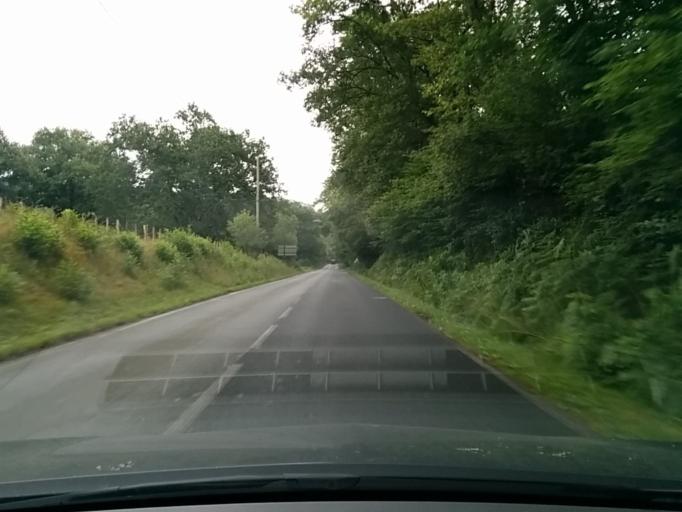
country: FR
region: Aquitaine
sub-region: Departement des Pyrenees-Atlantiques
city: Saint-Pee-sur-Nivelle
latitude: 43.3173
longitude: -1.5299
